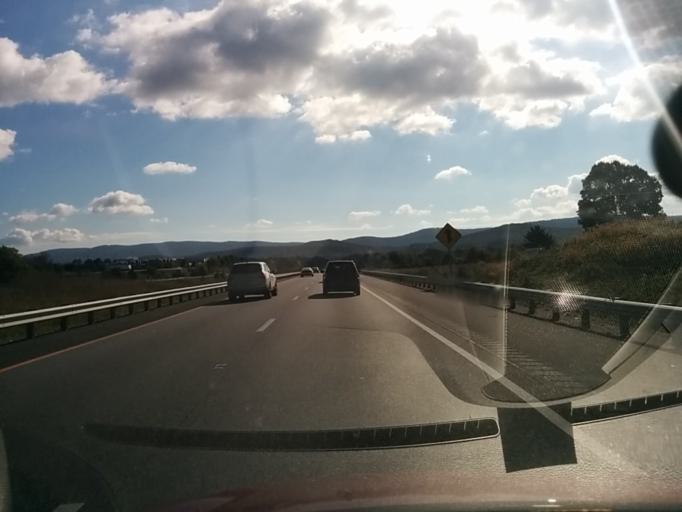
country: US
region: Virginia
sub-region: Augusta County
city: Lyndhurst
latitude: 38.0606
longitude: -78.9401
